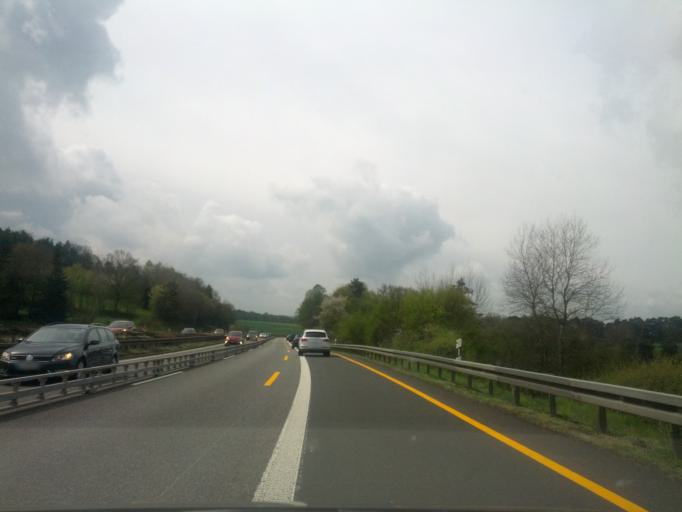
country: DE
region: Hesse
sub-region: Regierungsbezirk Kassel
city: Ottrau
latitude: 50.7668
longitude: 9.3757
